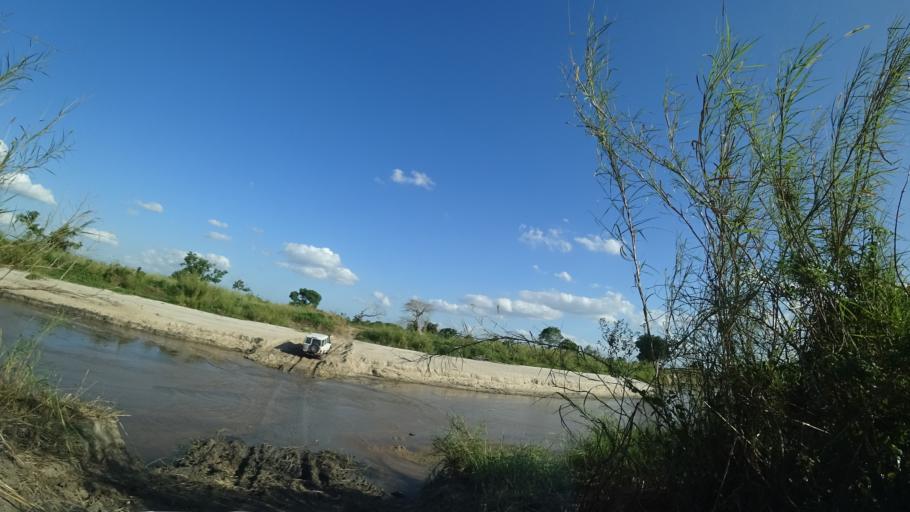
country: MZ
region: Sofala
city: Dondo
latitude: -19.3588
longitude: 34.5896
